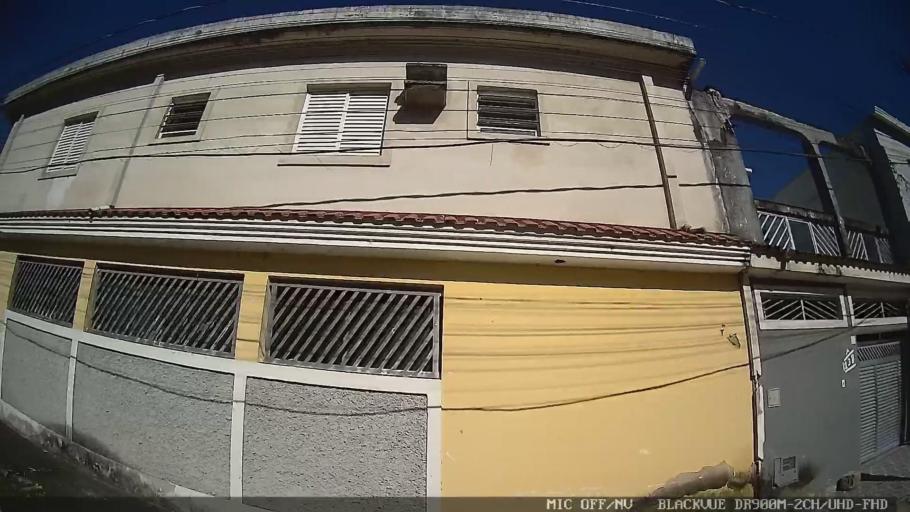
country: BR
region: Sao Paulo
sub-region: Santos
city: Santos
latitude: -23.9325
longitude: -46.2885
